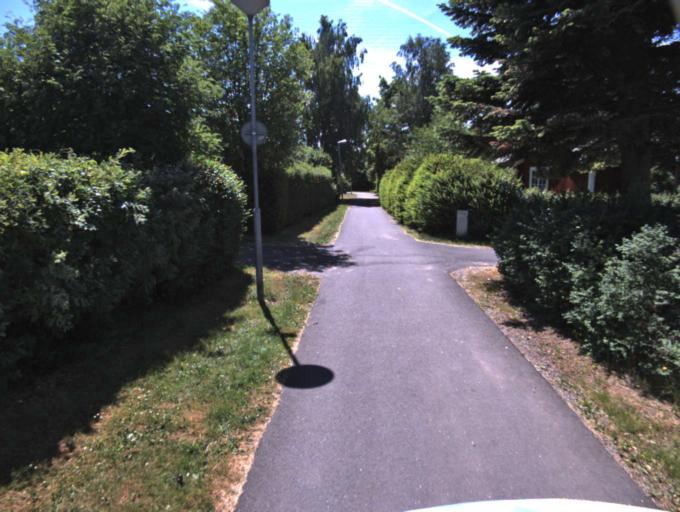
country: SE
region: Skane
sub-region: Kristianstads Kommun
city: Onnestad
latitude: 56.0533
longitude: 14.0199
